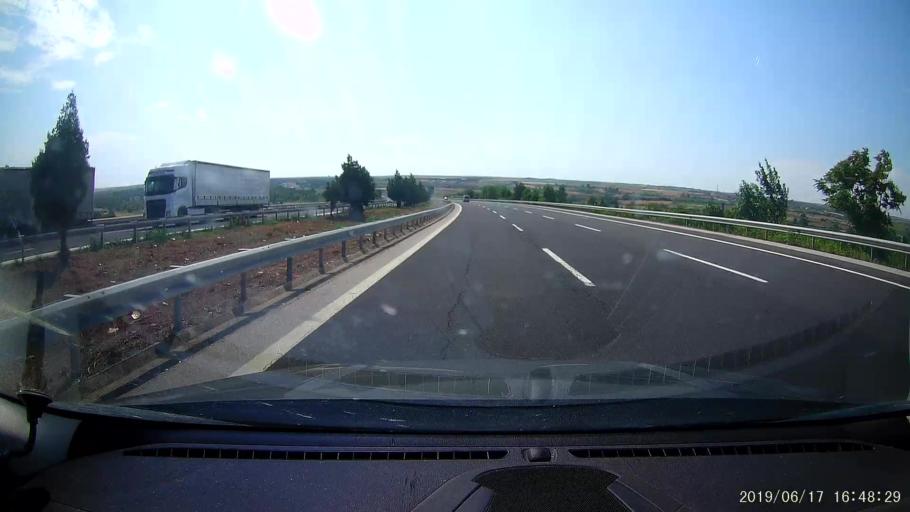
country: TR
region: Kirklareli
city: Babaeski
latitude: 41.5063
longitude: 27.1410
